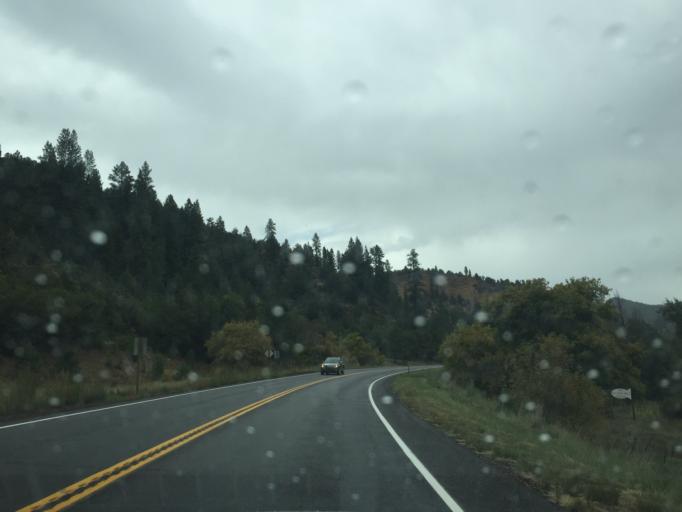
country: US
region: Utah
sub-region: Kane County
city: Kanab
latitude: 37.3692
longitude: -112.5947
